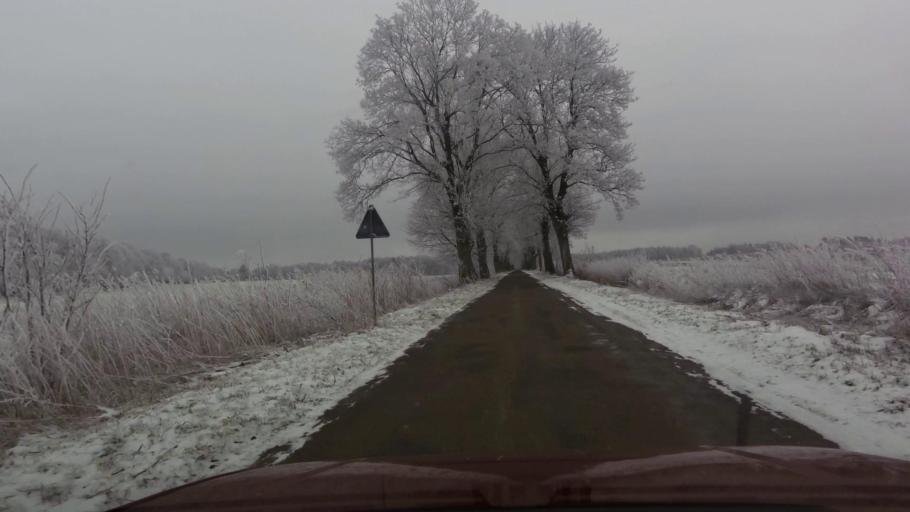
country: PL
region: West Pomeranian Voivodeship
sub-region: Powiat swidwinski
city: Rabino
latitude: 53.8001
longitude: 15.9977
